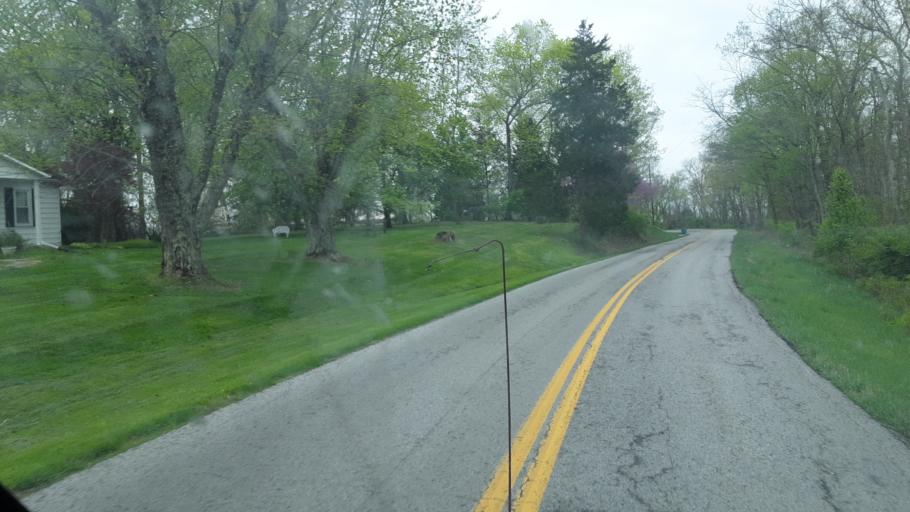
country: US
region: Kentucky
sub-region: Grant County
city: Dry Ridge
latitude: 38.6580
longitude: -84.7012
